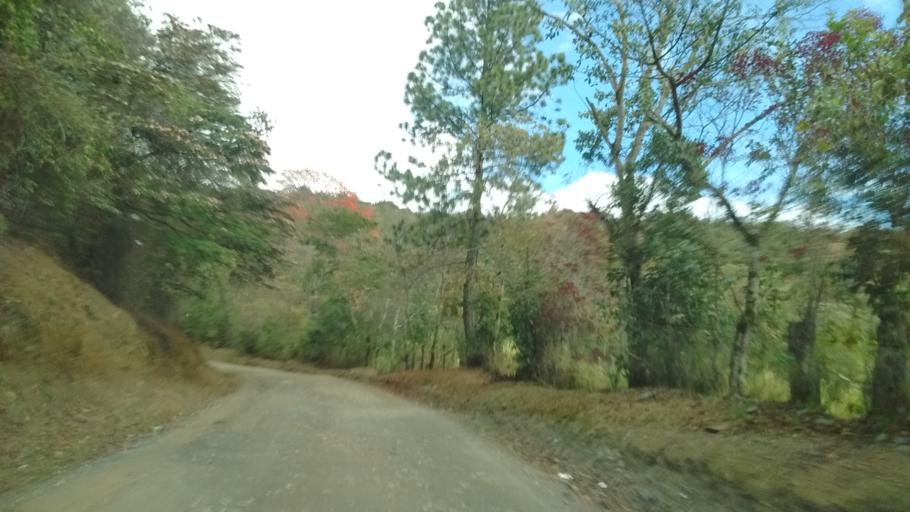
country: CO
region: Cauca
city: Almaguer
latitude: 1.8569
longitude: -76.9303
